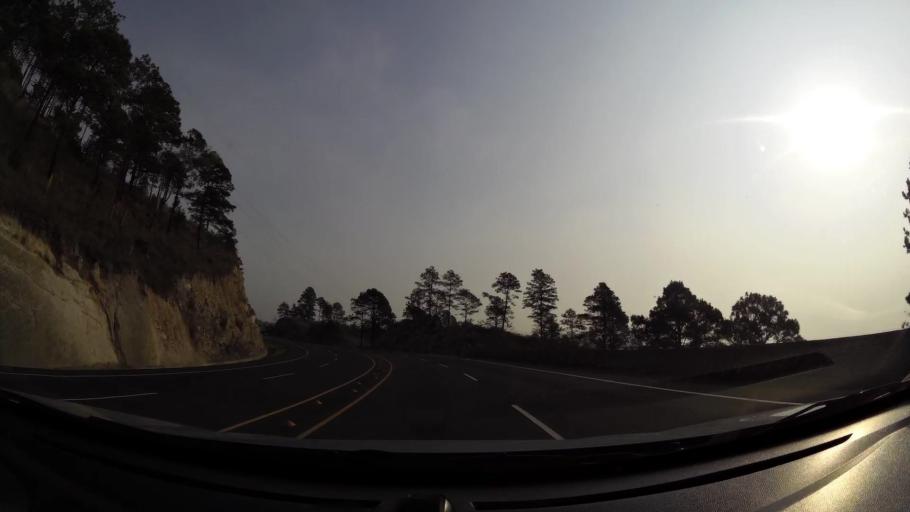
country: HN
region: Francisco Morazan
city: Zambrano
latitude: 14.2479
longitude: -87.3757
